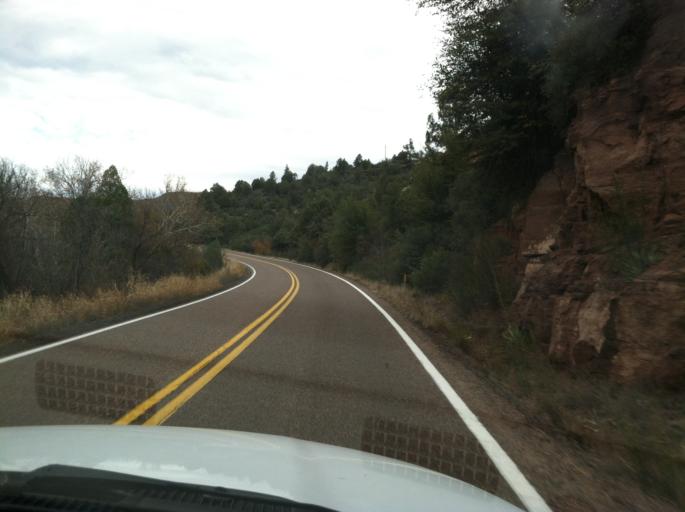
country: US
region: Arizona
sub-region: Gila County
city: Payson
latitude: 34.3039
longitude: -111.3591
